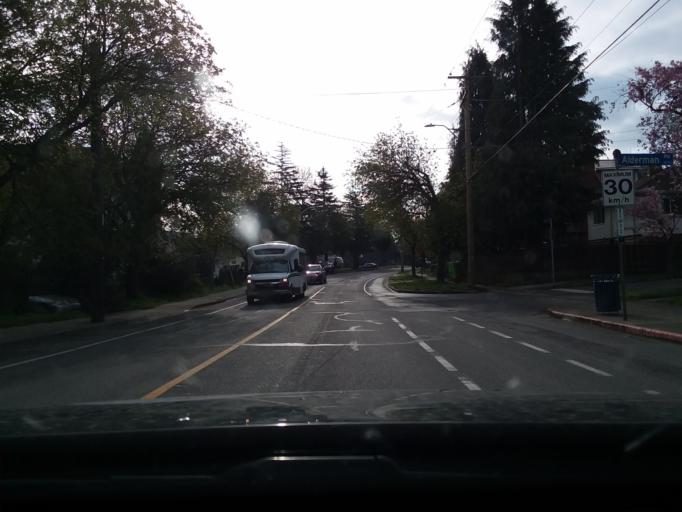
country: CA
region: British Columbia
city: Victoria
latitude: 48.4388
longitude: -123.3911
